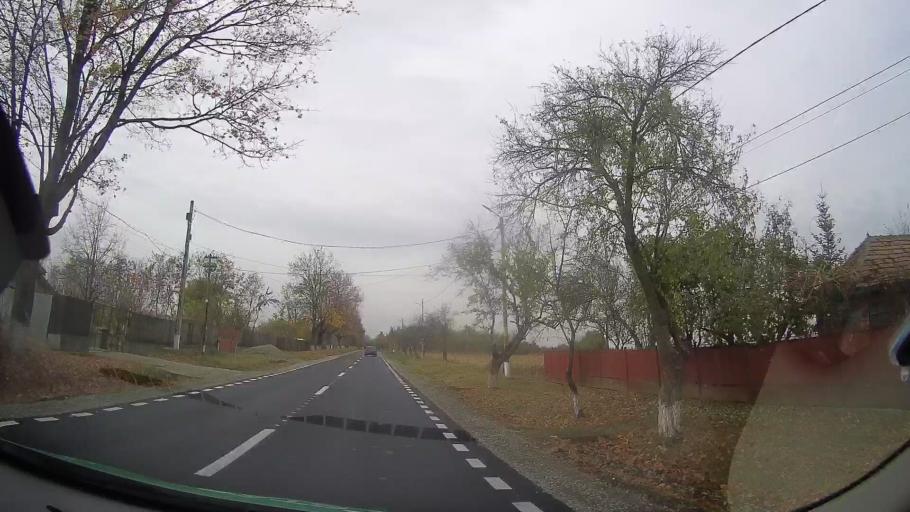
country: RO
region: Ilfov
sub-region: Comuna Nuci
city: Nuci
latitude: 44.7182
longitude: 26.3092
